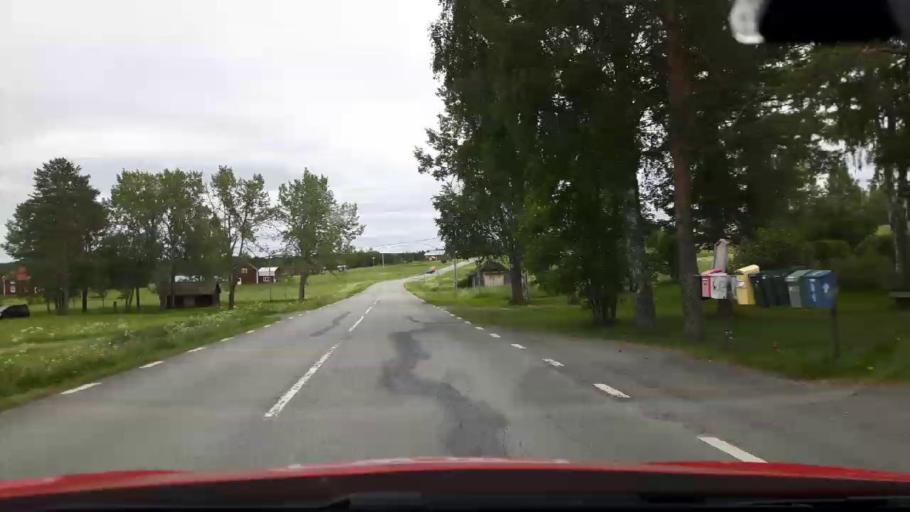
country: SE
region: Jaemtland
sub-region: Stroemsunds Kommun
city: Stroemsund
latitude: 63.5599
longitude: 15.3996
